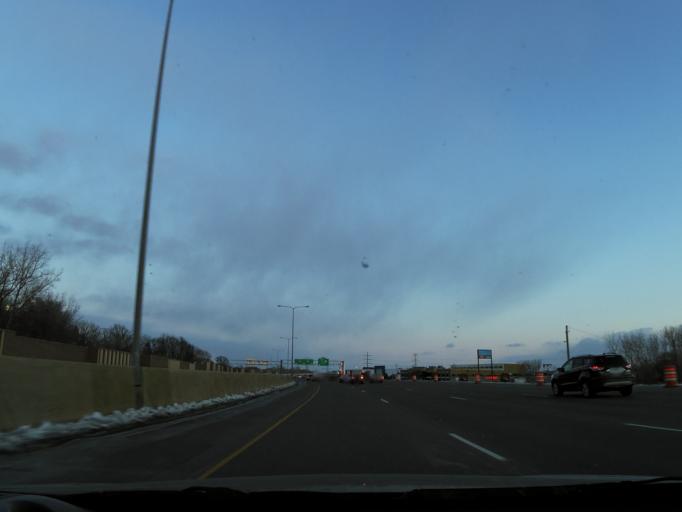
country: US
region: Minnesota
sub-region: Ramsey County
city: Little Canada
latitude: 45.0417
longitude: -93.1008
